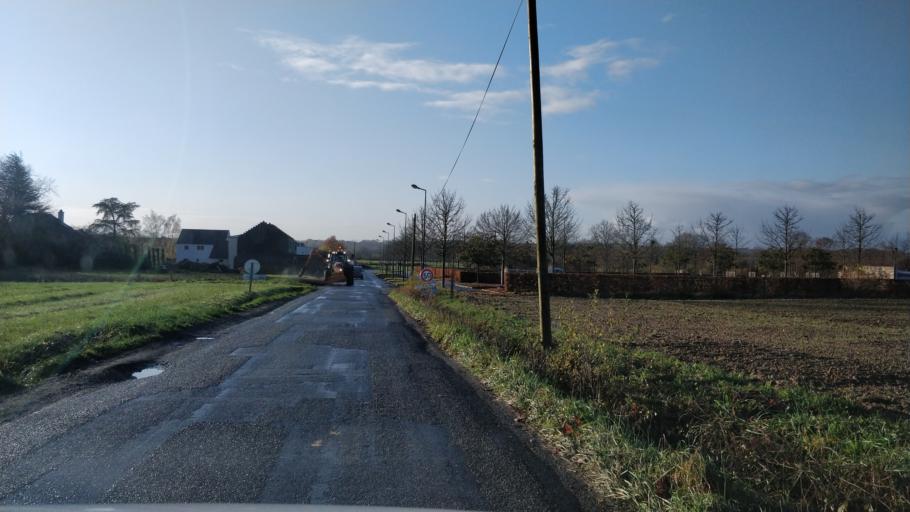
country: FR
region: Brittany
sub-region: Departement d'Ille-et-Vilaine
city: Chavagne
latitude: 48.0553
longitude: -1.8000
